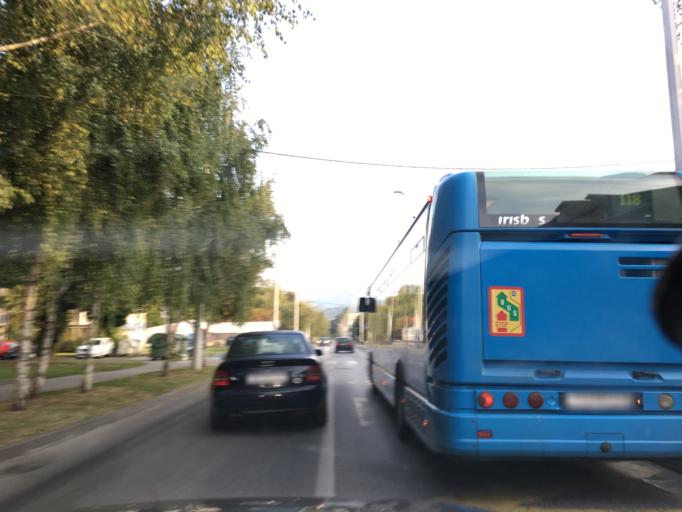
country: HR
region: Grad Zagreb
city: Jankomir
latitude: 45.8051
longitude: 15.9301
